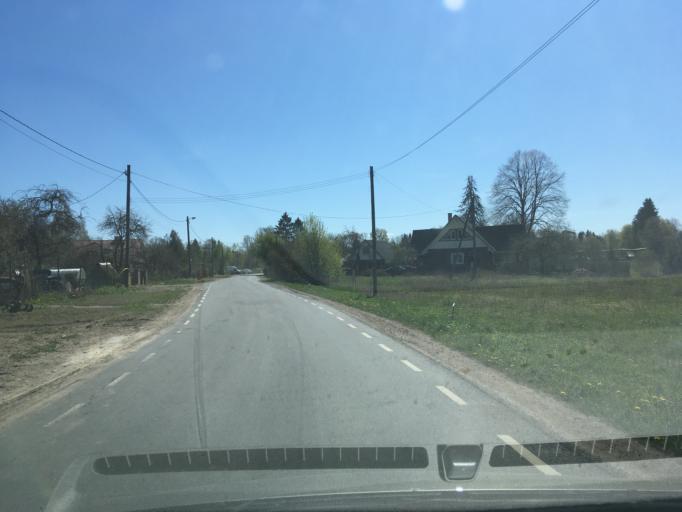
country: EE
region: Harju
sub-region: Raasiku vald
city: Arukula
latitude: 59.3741
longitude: 25.0777
